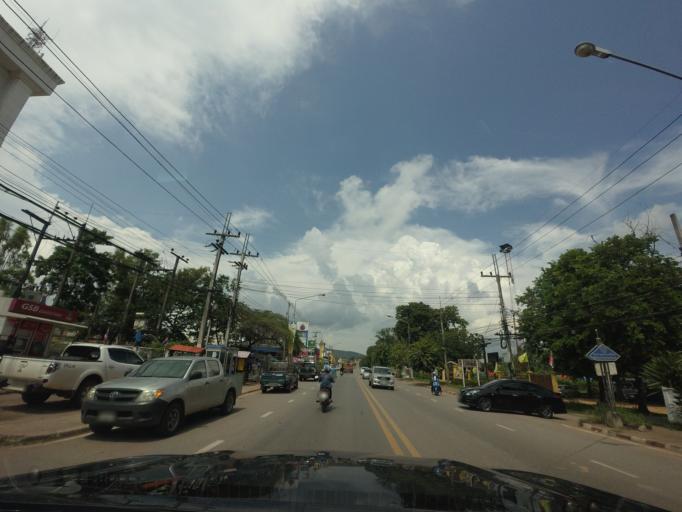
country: TH
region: Khon Kaen
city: Phu Wiang
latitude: 16.6549
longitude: 102.3745
